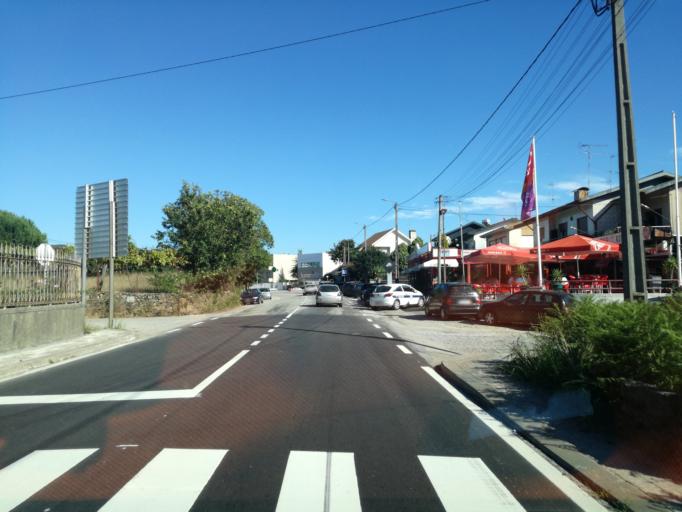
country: PT
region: Porto
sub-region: Valongo
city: Alfena
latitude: 41.2595
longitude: -8.4875
